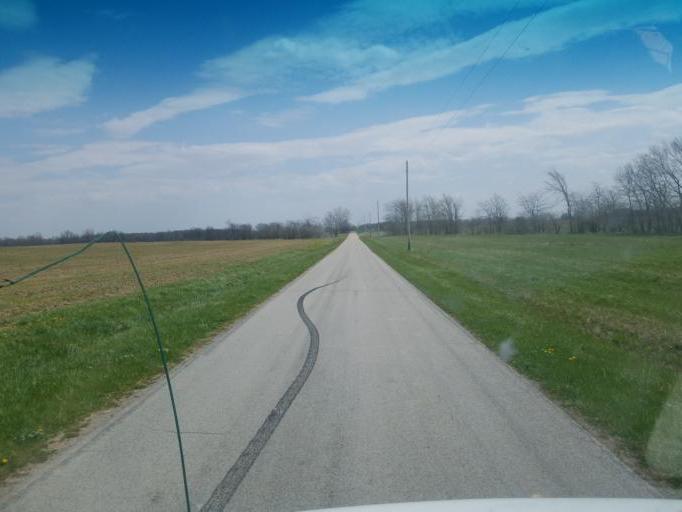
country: US
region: Ohio
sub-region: Hardin County
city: Forest
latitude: 40.7742
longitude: -83.4482
